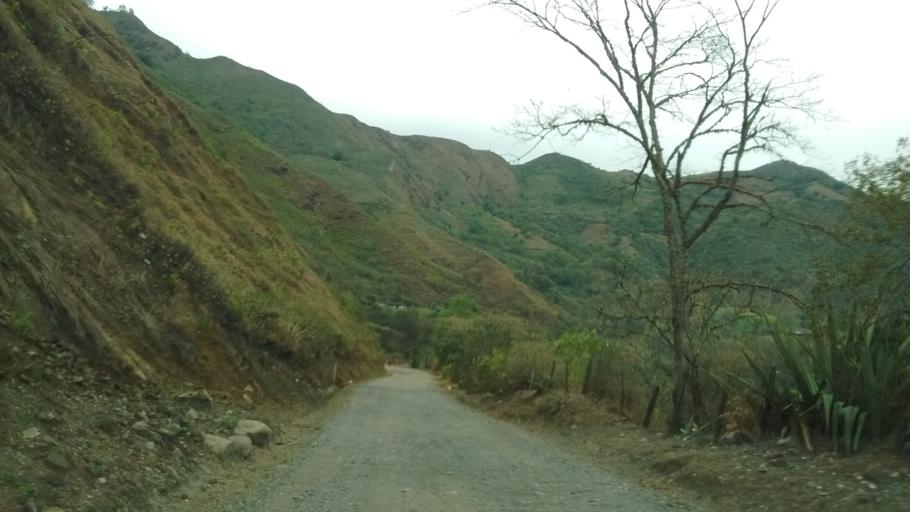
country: CO
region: Cauca
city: Almaguer
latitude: 1.8447
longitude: -76.9134
